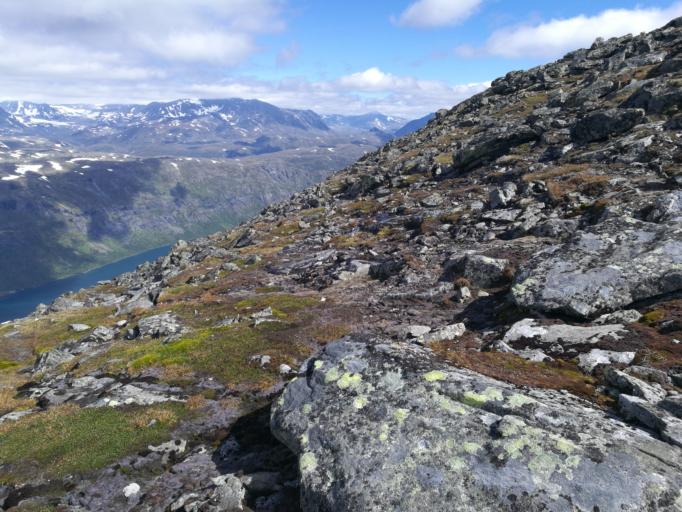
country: NO
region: Oppland
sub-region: Vang
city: Vang
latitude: 61.4272
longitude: 8.5006
